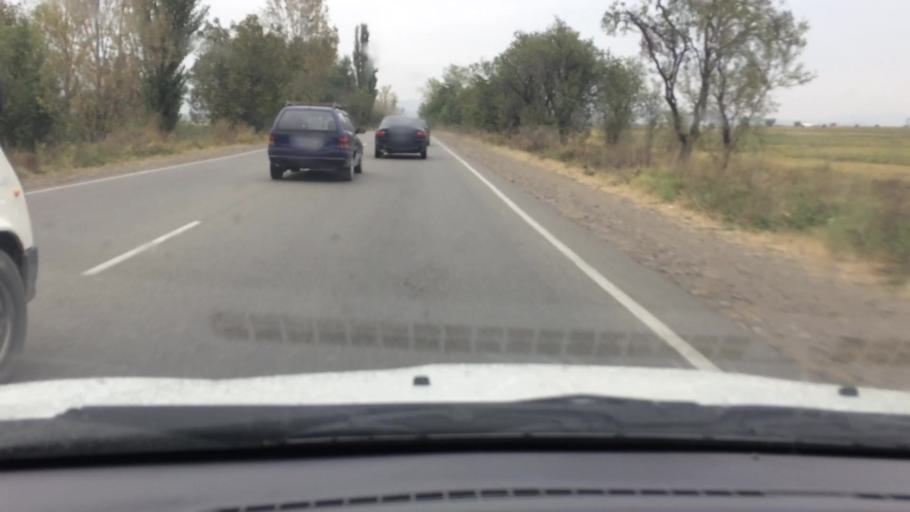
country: GE
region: Kvemo Kartli
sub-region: Marneuli
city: Marneuli
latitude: 41.5512
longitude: 44.7763
